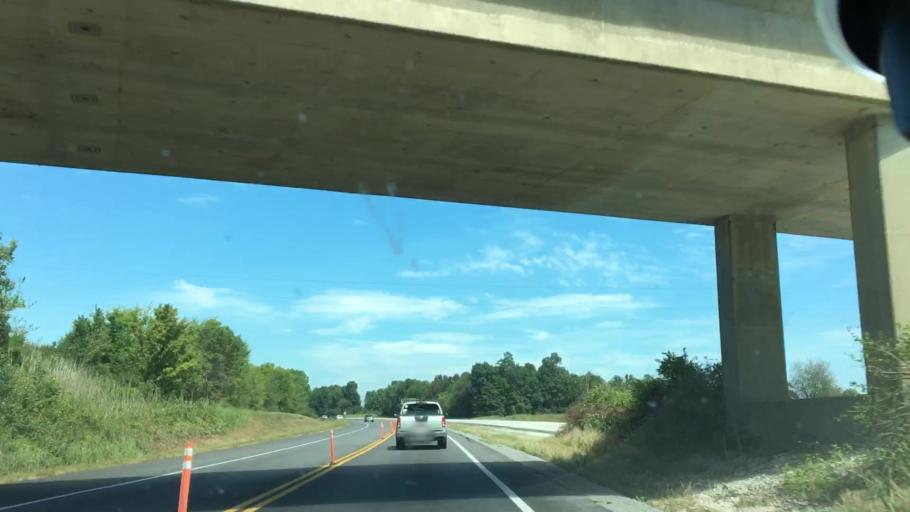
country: US
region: Kentucky
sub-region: Christian County
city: Hopkinsville
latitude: 37.0086
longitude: -87.4591
